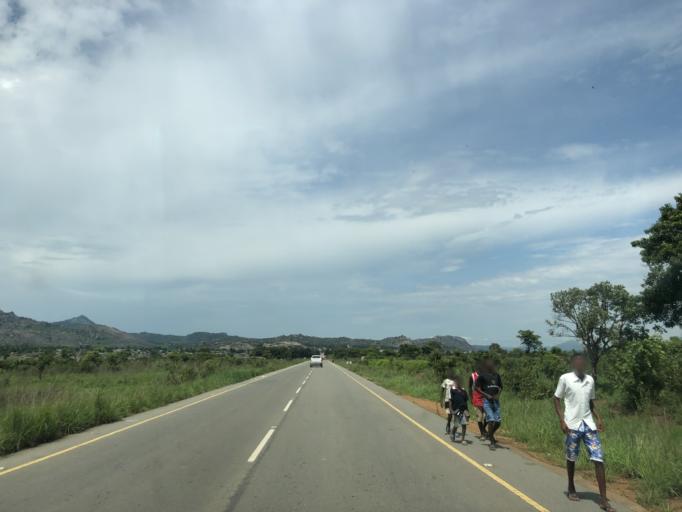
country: AO
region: Cuanza Sul
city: Quibala
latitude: -10.7348
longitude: 15.0036
